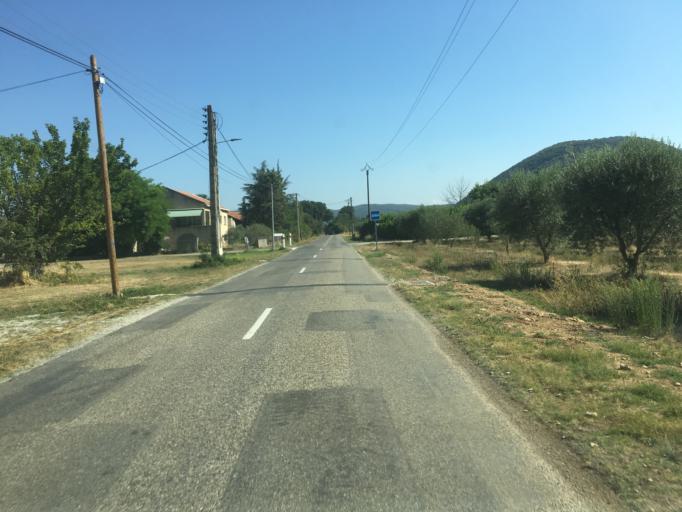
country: FR
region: Provence-Alpes-Cote d'Azur
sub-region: Departement des Alpes-de-Haute-Provence
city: Villeneuve
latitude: 43.8666
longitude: 5.8974
